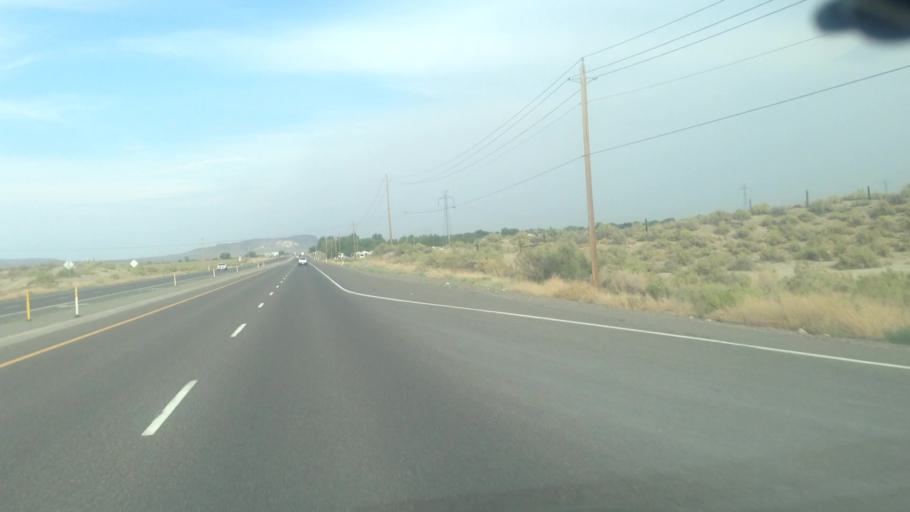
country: US
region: Nevada
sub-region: Lyon County
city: Fernley
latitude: 39.5943
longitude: -119.1675
